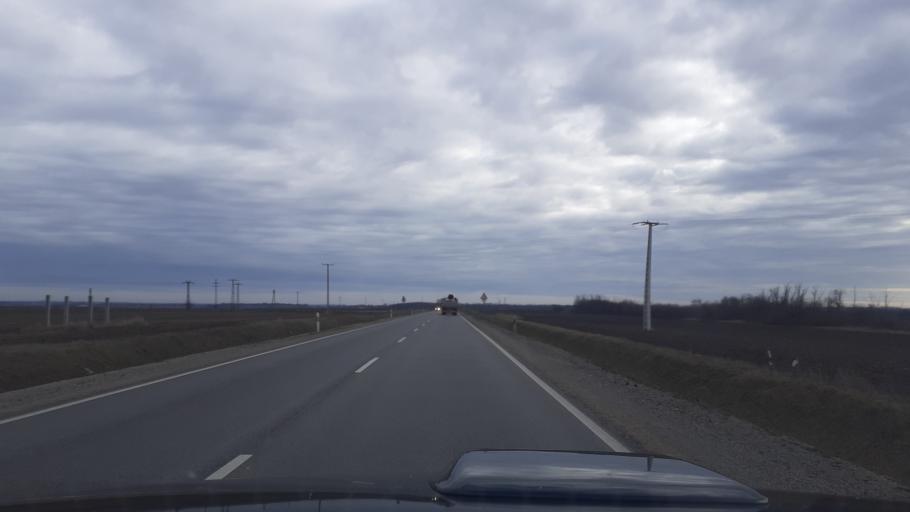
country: HU
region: Fejer
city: Seregelyes
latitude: 47.1376
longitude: 18.5381
